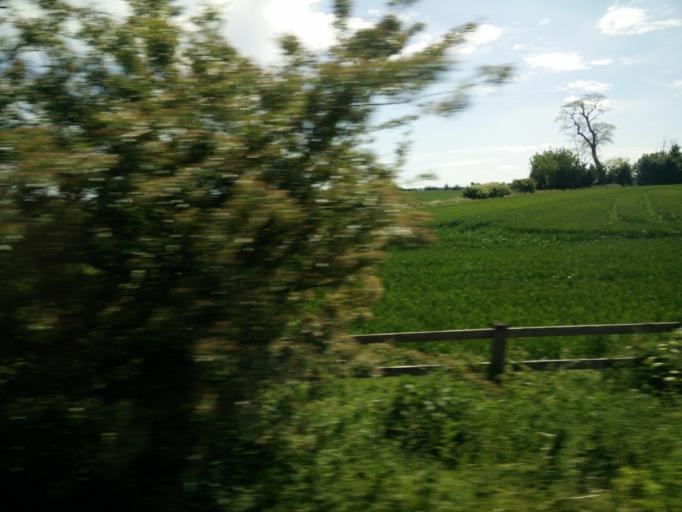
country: GB
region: England
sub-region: Hertfordshire
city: Hitchin
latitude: 51.9434
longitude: -0.2945
